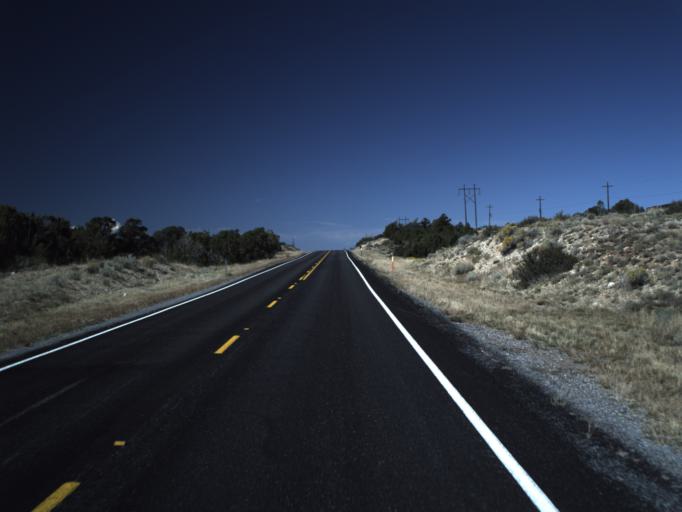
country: US
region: Utah
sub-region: Iron County
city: Cedar City
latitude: 37.6111
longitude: -113.3805
